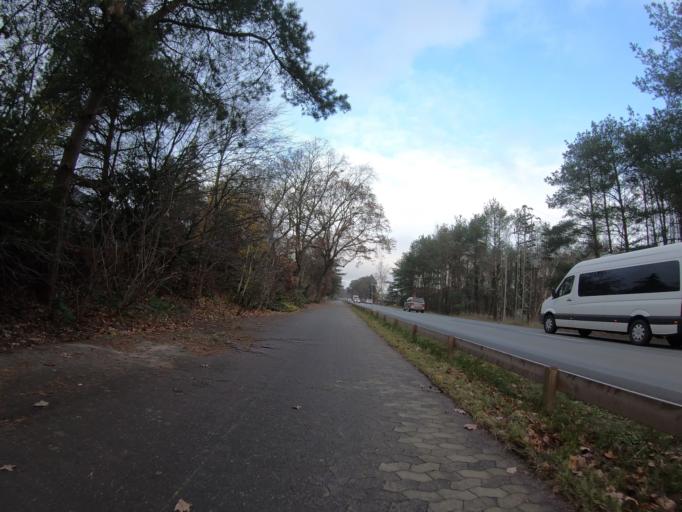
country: DE
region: Lower Saxony
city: Wagenhoff
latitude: 52.5574
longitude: 10.5135
